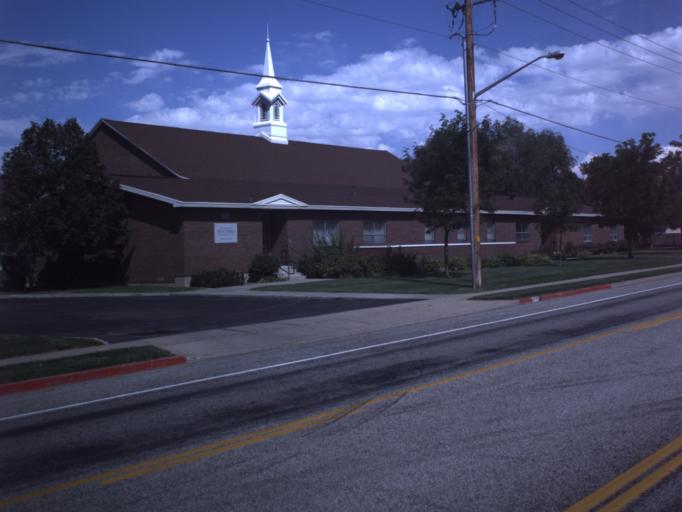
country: US
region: Utah
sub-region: Weber County
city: Farr West
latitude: 41.2963
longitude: -112.0277
